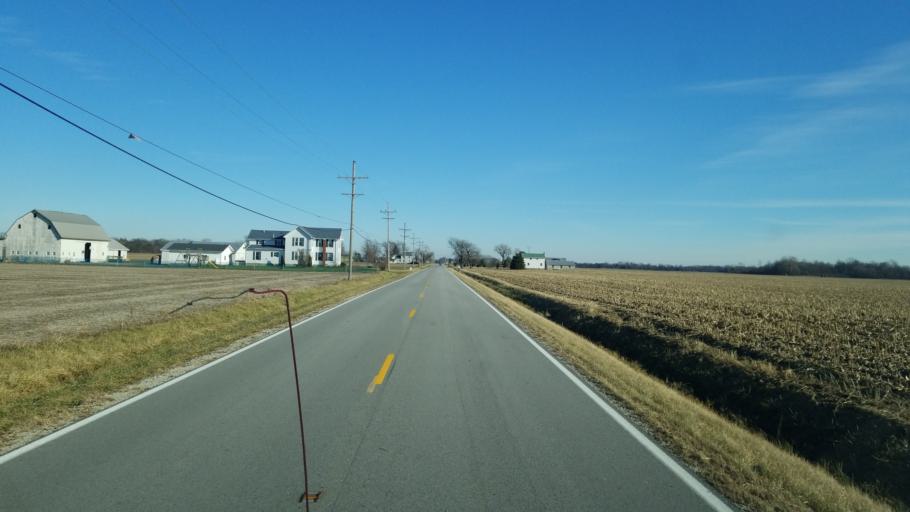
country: US
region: Ohio
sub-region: Sandusky County
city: Stony Prairie
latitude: 41.3489
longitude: -83.2180
